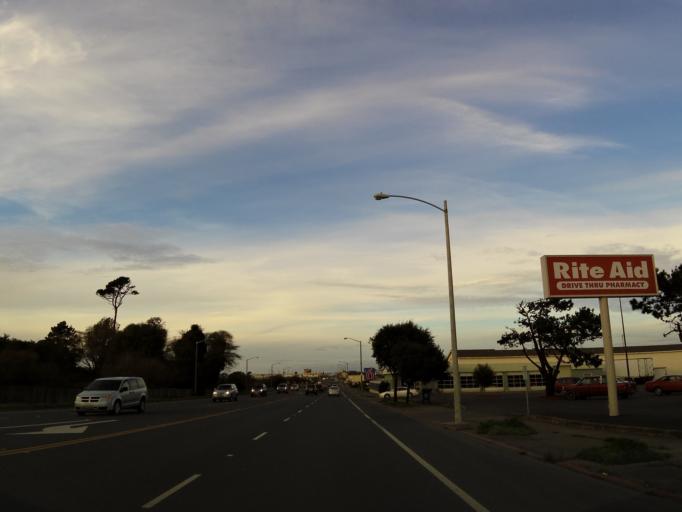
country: US
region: California
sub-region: Mendocino County
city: Fort Bragg
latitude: 39.4365
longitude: -123.8061
